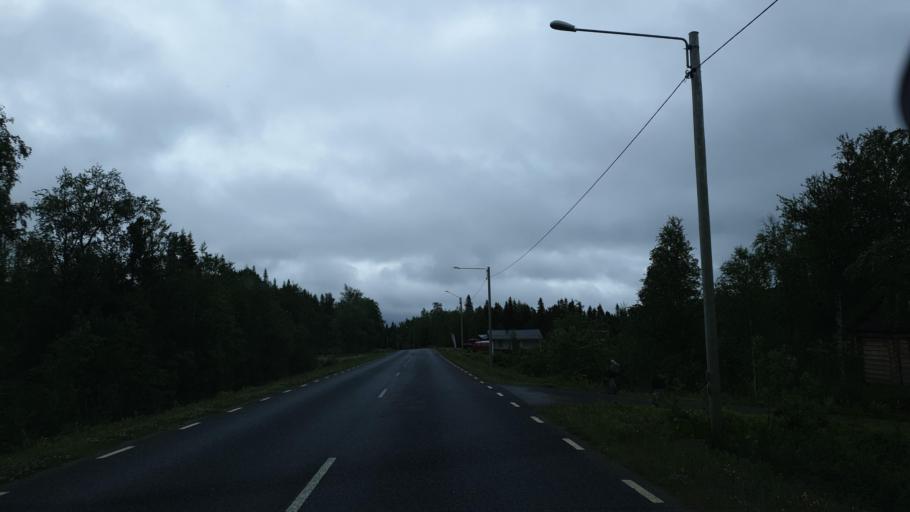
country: SE
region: Vaesterbotten
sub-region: Vilhelmina Kommun
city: Sjoberg
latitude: 65.2519
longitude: 15.5609
